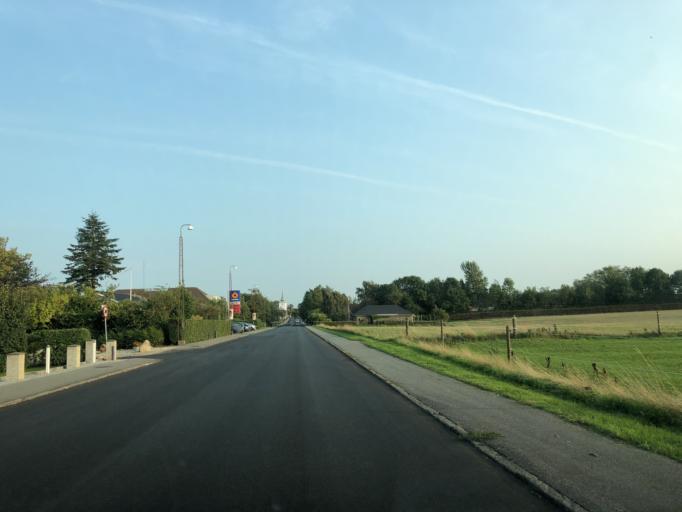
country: DK
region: South Denmark
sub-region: Vejle Kommune
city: Jelling
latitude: 55.7070
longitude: 9.3767
